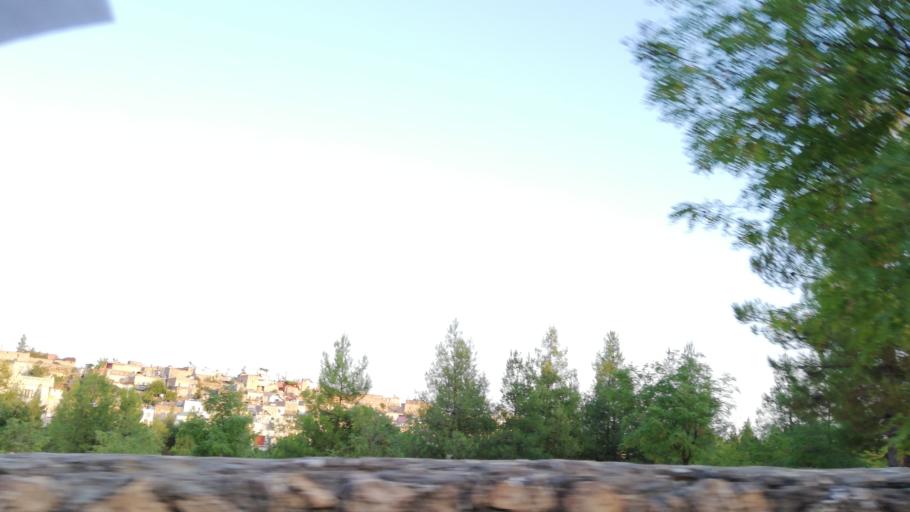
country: TR
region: Mardin
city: Kindirip
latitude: 37.4495
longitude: 41.2181
